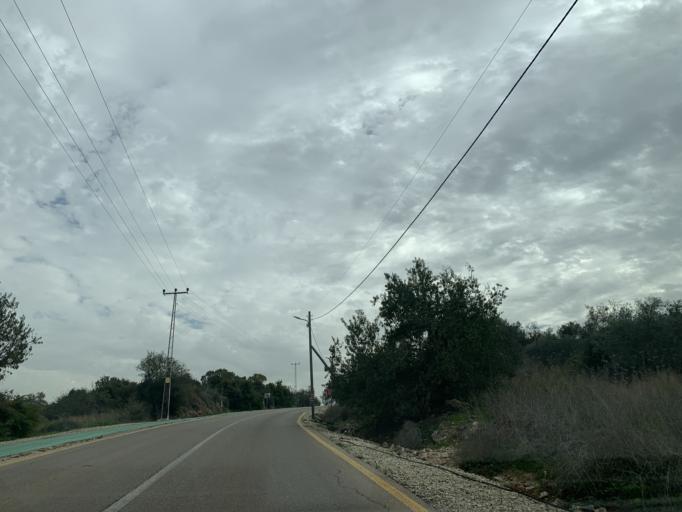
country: IL
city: Nirit
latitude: 32.1451
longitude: 34.9826
